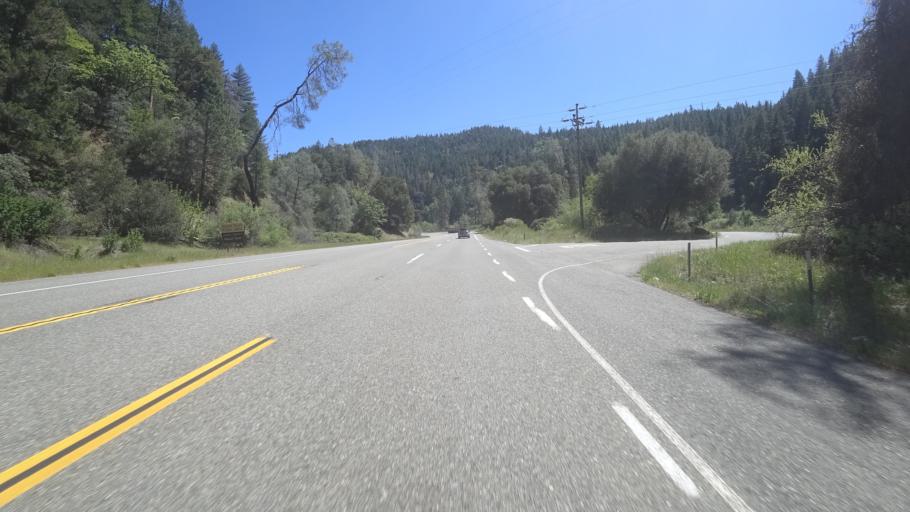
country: US
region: California
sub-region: Trinity County
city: Hayfork
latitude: 40.7374
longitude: -123.2346
